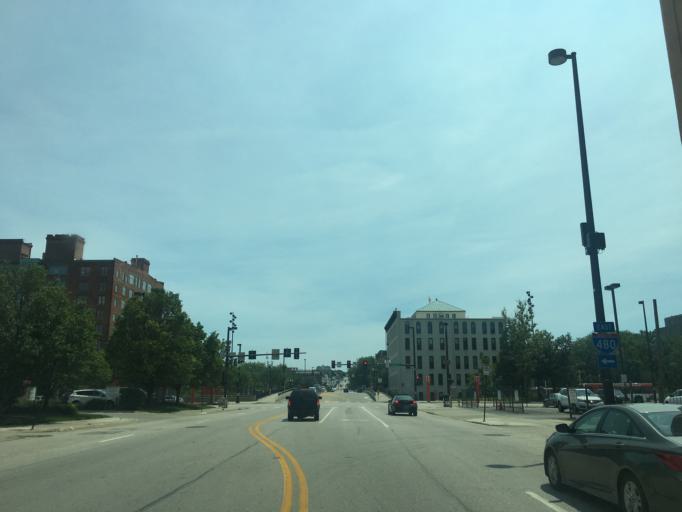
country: US
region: Nebraska
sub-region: Douglas County
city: Omaha
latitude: 41.2594
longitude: -95.9293
